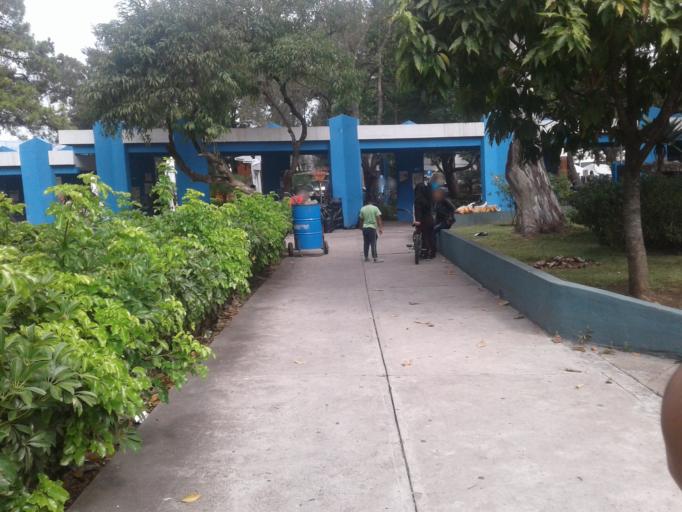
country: GT
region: Guatemala
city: Santa Catarina Pinula
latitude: 14.5866
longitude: -90.5524
